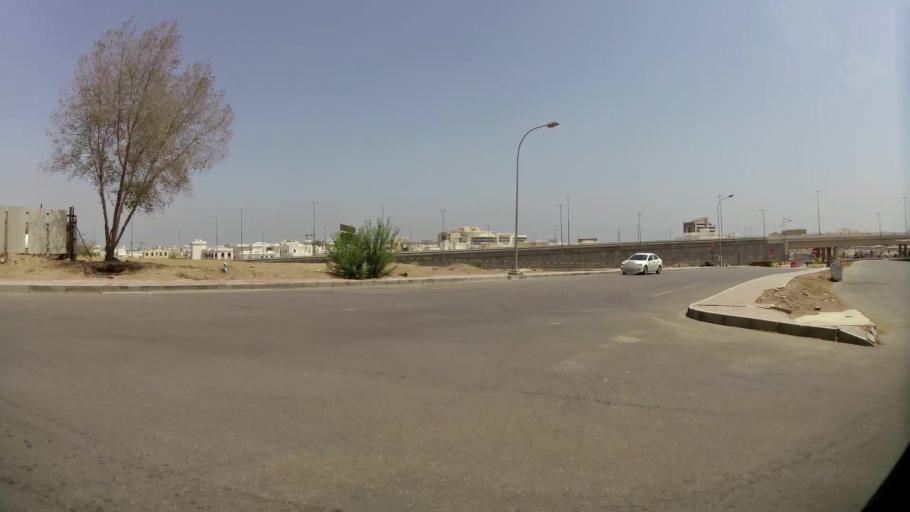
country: OM
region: Muhafazat Masqat
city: Bawshar
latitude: 23.5896
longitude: 58.4428
